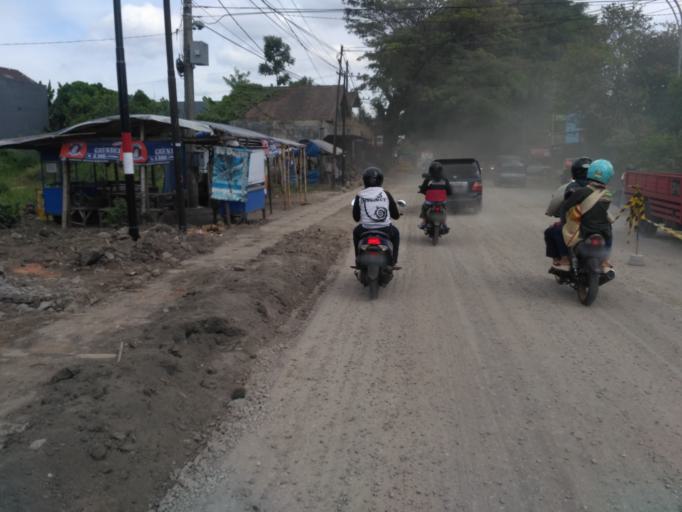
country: ID
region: East Java
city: Kebonsari
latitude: -8.0272
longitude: 112.6273
